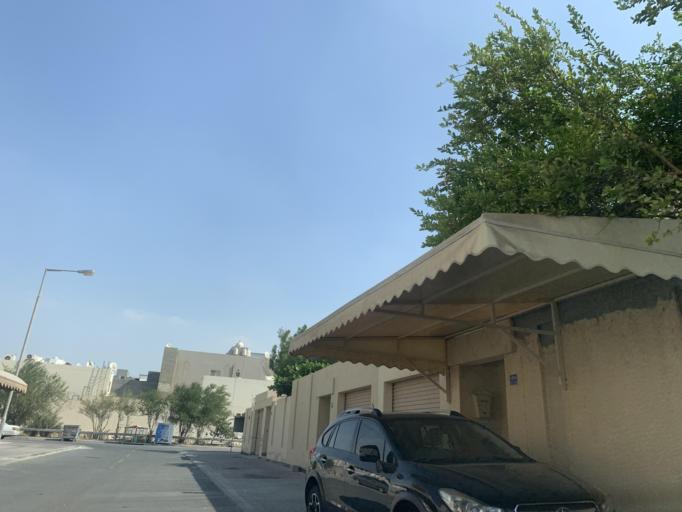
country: BH
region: Central Governorate
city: Madinat Hamad
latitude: 26.1253
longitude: 50.4893
